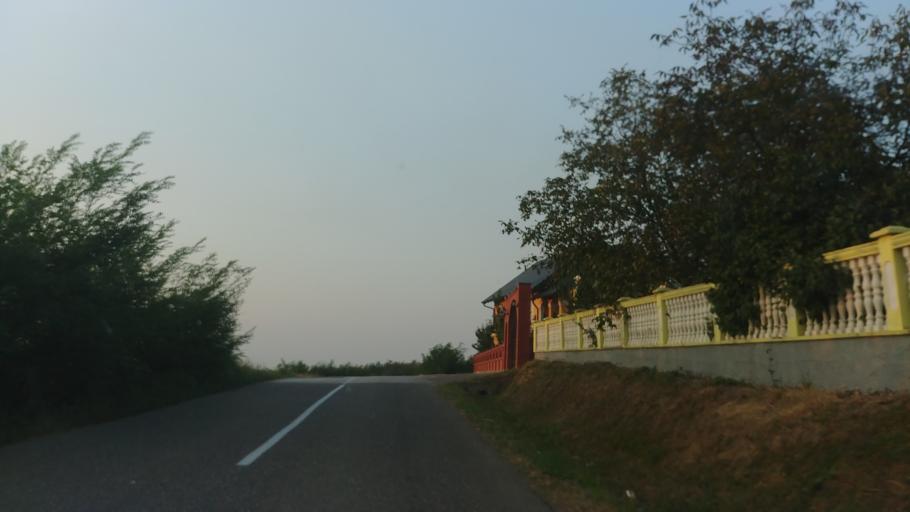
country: BA
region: Republika Srpska
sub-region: Opstina Ugljevik
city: Ugljevik
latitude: 44.7140
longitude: 18.9896
